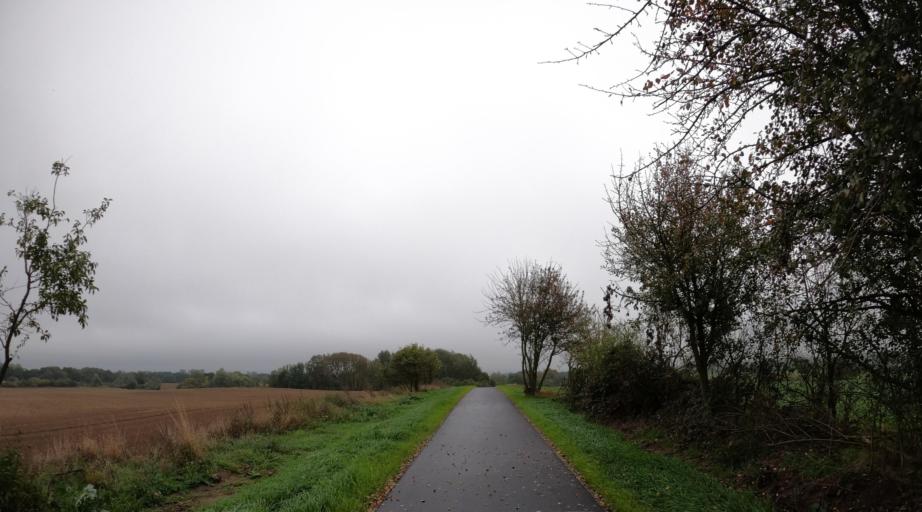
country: PL
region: West Pomeranian Voivodeship
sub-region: Powiat mysliborski
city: Mysliborz
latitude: 52.9224
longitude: 14.7376
